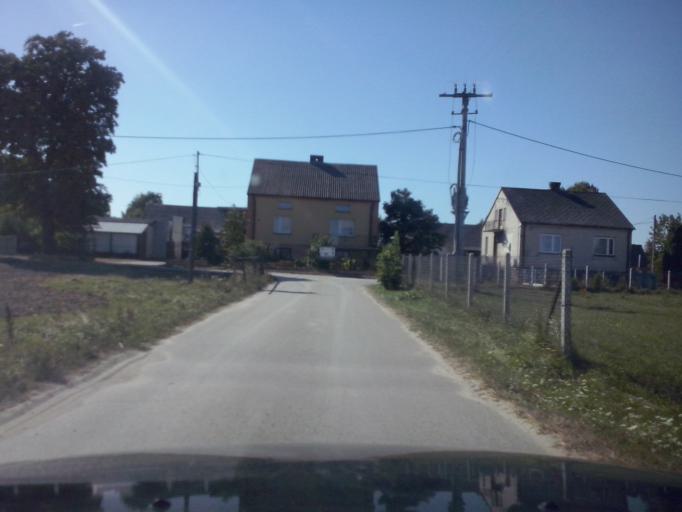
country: PL
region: Swietokrzyskie
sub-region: Powiat kielecki
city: Chmielnik
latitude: 50.6144
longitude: 20.7051
